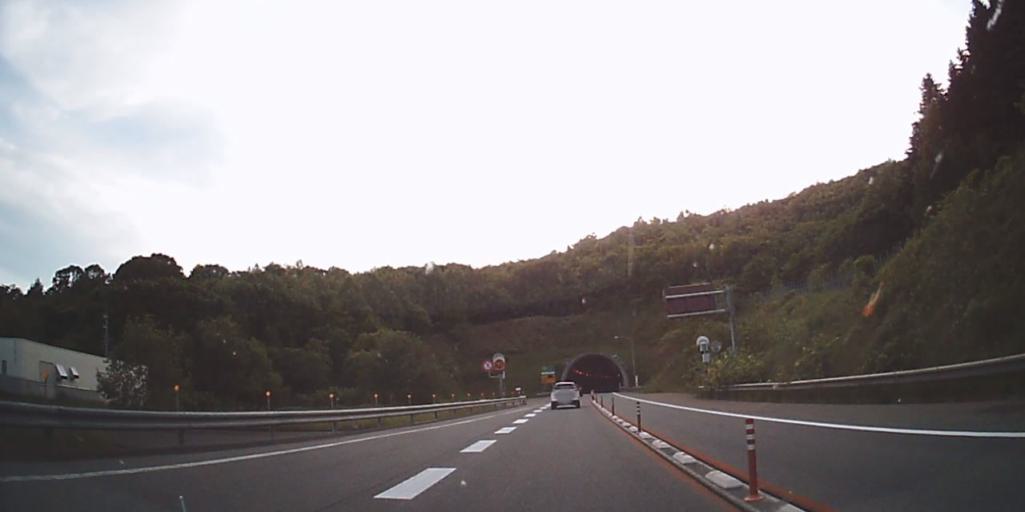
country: JP
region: Hokkaido
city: Date
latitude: 42.5583
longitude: 140.7679
